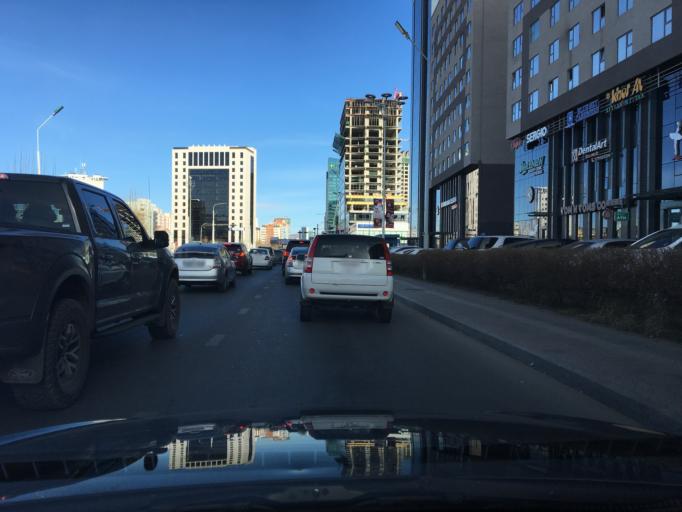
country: MN
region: Ulaanbaatar
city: Ulaanbaatar
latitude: 47.8980
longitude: 106.9087
